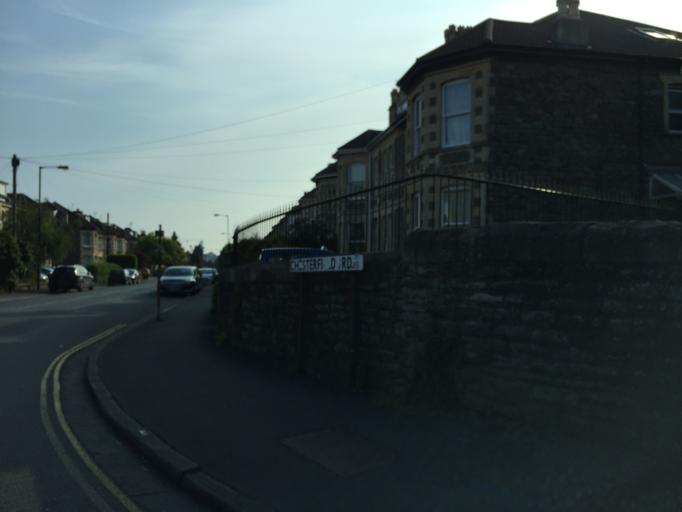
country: GB
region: England
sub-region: Bristol
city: Bristol
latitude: 51.4711
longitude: -2.5851
